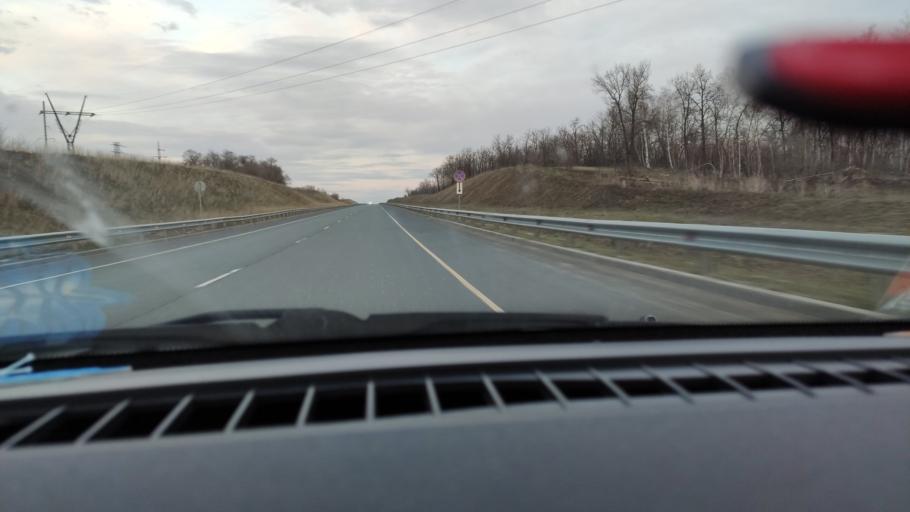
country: RU
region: Saratov
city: Yelshanka
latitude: 51.8219
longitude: 46.3304
